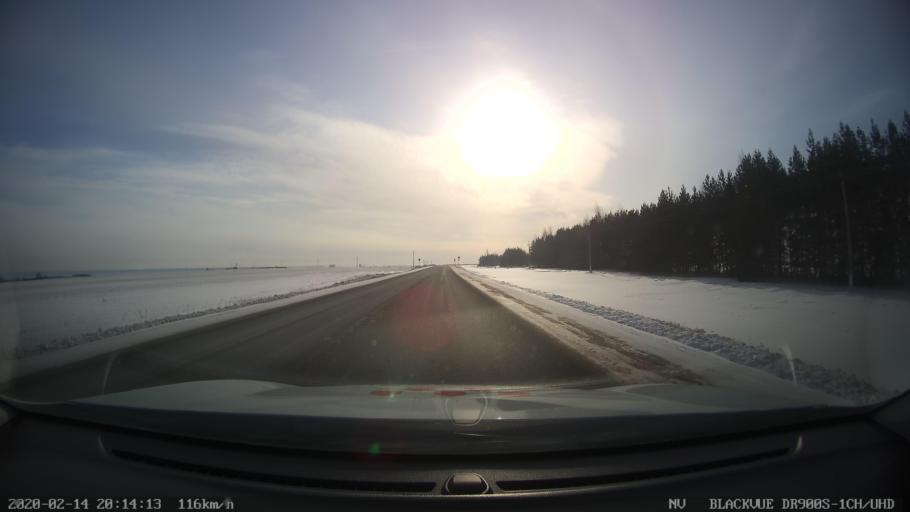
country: RU
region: Tatarstan
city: Verkhniy Uslon
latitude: 55.6480
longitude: 48.8719
